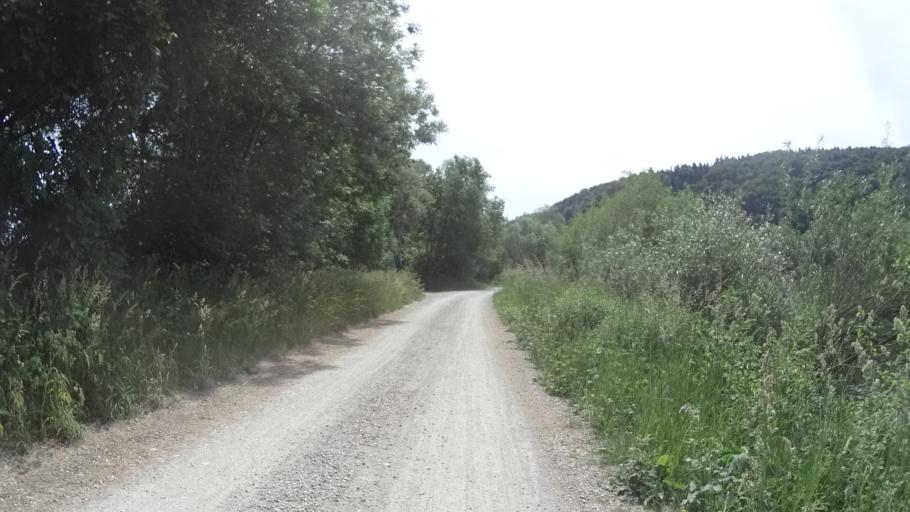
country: DE
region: Bavaria
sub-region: Lower Bavaria
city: Saal
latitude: 48.9062
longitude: 11.9492
